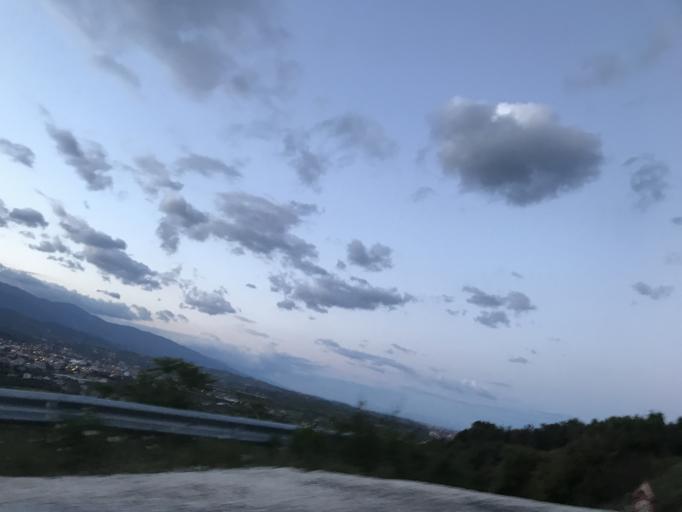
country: TR
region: Hatay
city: Uzunbag
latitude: 36.1205
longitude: 36.0447
